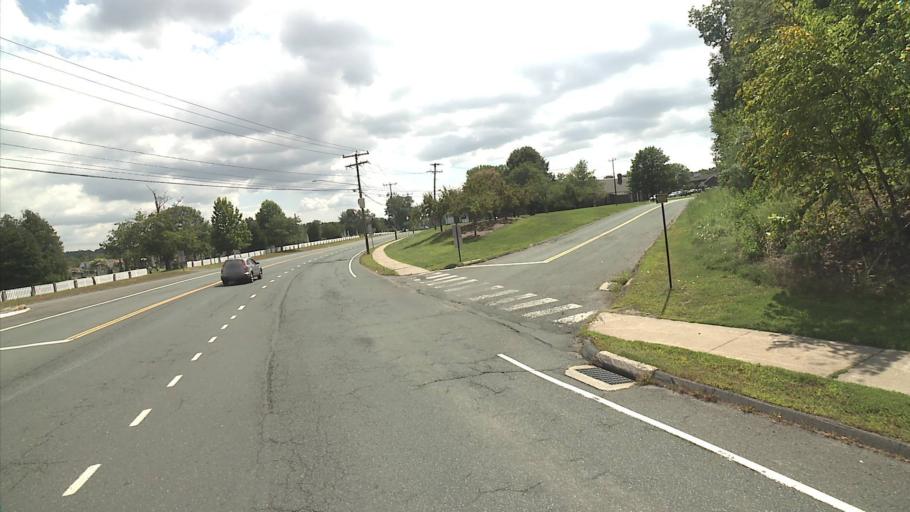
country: US
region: Connecticut
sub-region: Hartford County
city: Salmon Brook
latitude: 41.9562
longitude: -72.7937
